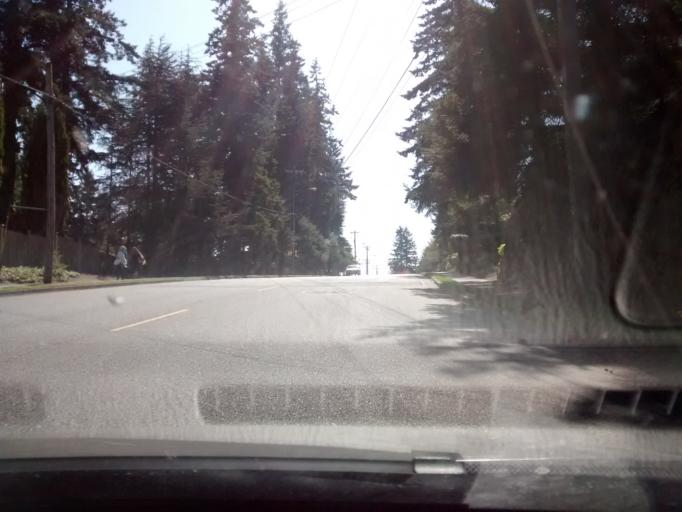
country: US
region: Washington
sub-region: Snohomish County
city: Esperance
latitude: 47.8097
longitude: -122.3489
